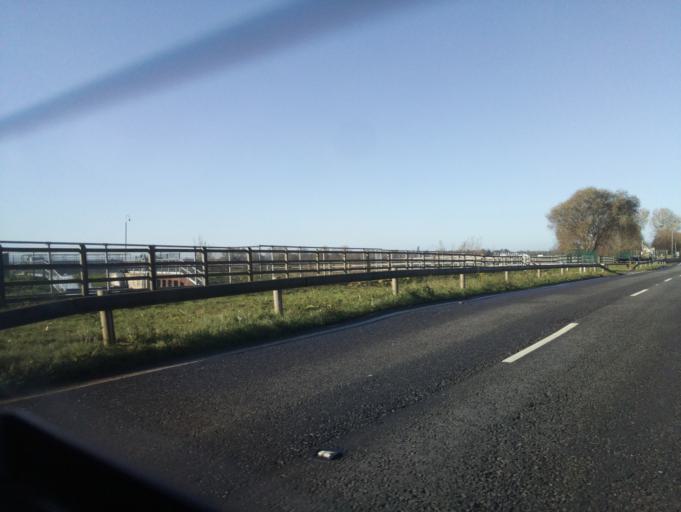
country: GB
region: England
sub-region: Somerset
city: Curry Rivel
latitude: 51.0796
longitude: -2.8676
